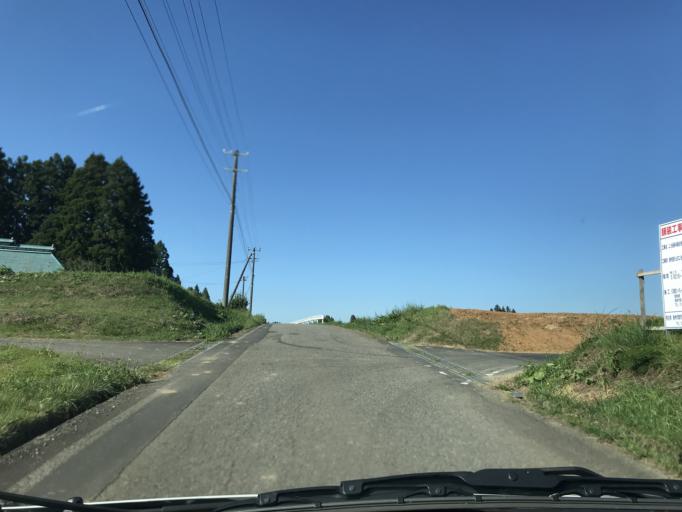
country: JP
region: Iwate
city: Mizusawa
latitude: 39.0722
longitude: 141.0470
